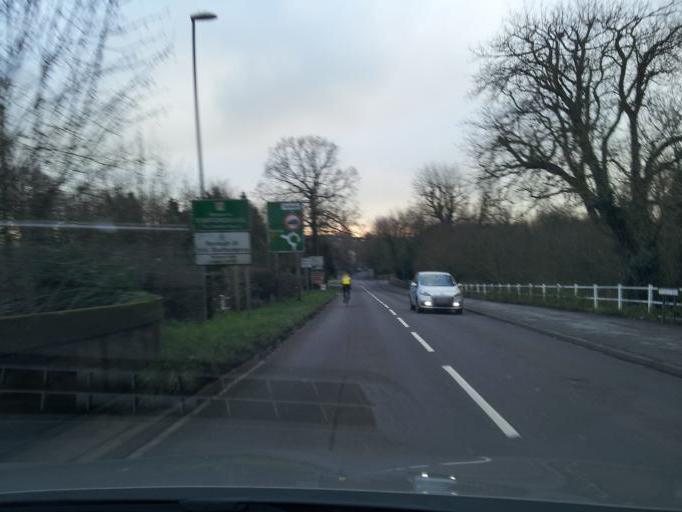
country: GB
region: England
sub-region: Staffordshire
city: Burton upon Trent
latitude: 52.8625
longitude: -1.6829
